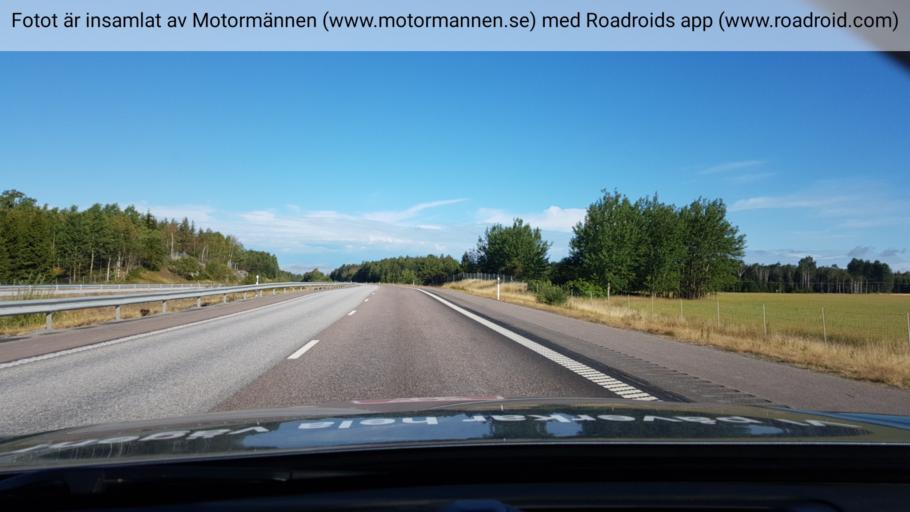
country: SE
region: Uppsala
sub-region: Habo Kommun
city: Balsta
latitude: 59.6044
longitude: 17.4328
